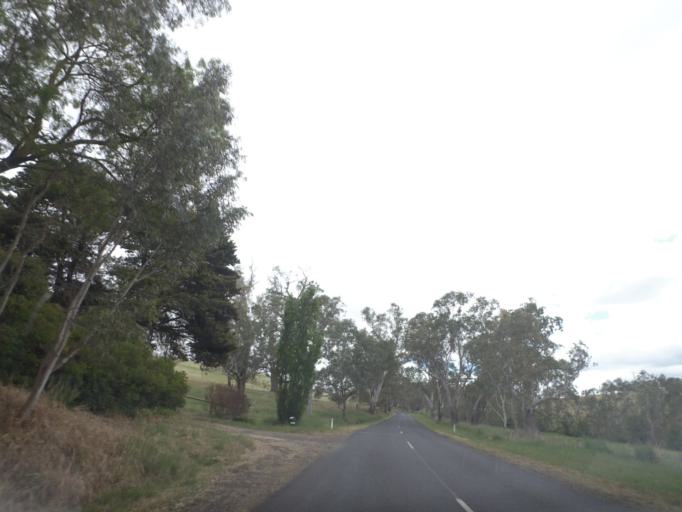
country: AU
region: Victoria
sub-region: Whittlesea
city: Whittlesea
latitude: -37.1951
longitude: 145.0381
